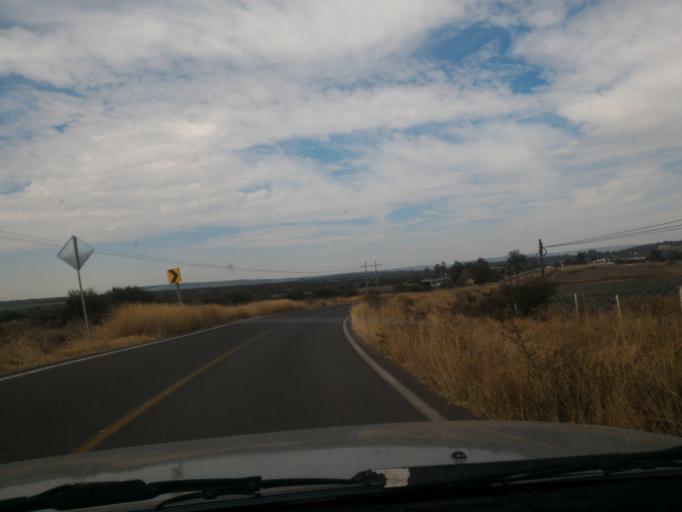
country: MX
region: Guanajuato
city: Ciudad Manuel Doblado
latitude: 20.8053
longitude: -101.9965
